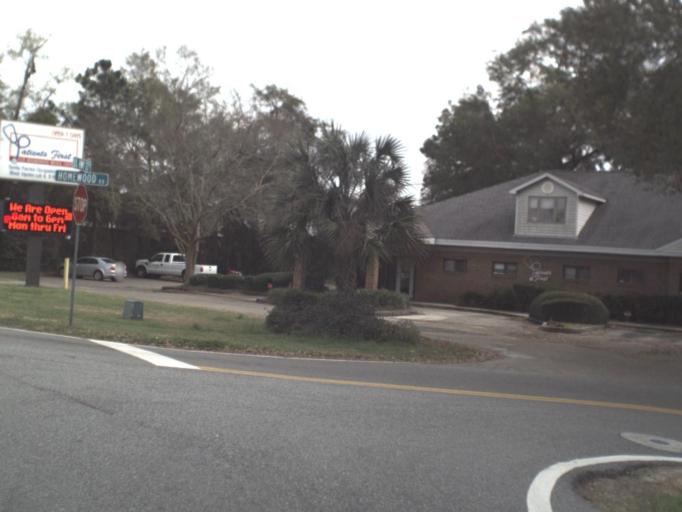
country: US
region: Florida
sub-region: Leon County
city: Tallahassee
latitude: 30.4883
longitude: -84.3199
